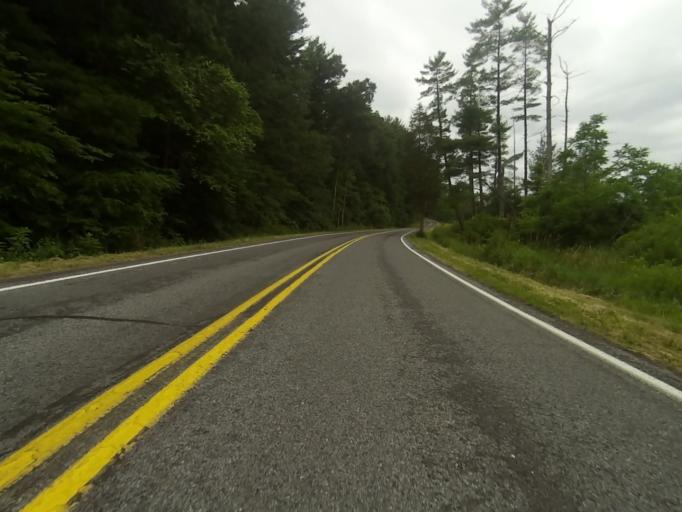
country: US
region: Pennsylvania
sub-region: Centre County
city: Stormstown
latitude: 40.7300
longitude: -77.9779
